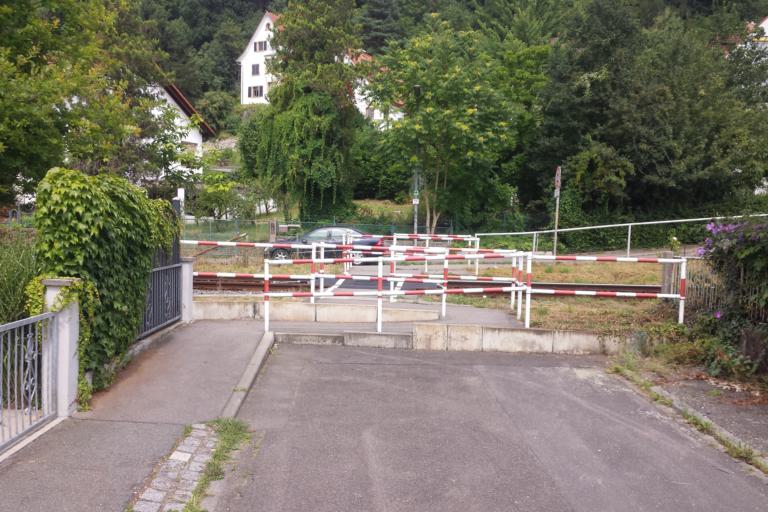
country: DE
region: Baden-Wuerttemberg
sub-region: Karlsruhe Region
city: Weinheim
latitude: 49.5582
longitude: 8.6752
